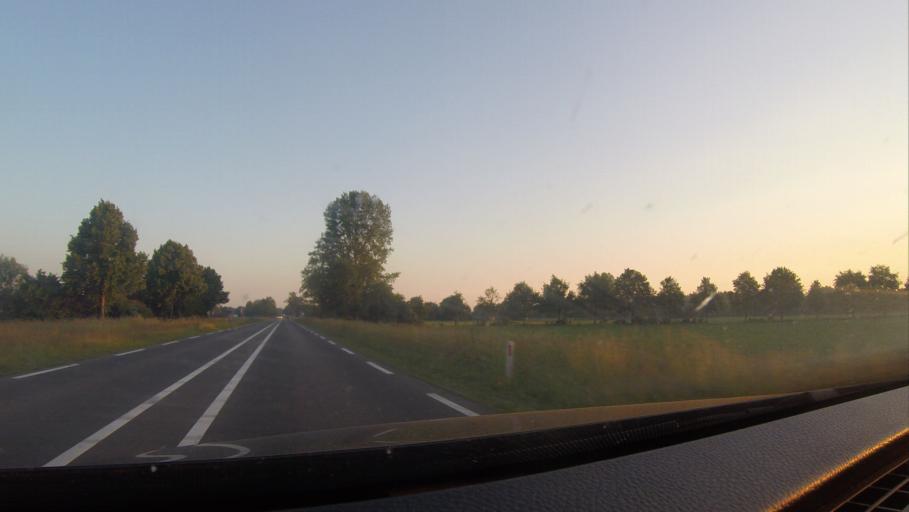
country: NL
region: Overijssel
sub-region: Gemeente Raalte
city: Heino
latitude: 52.4539
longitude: 6.2178
